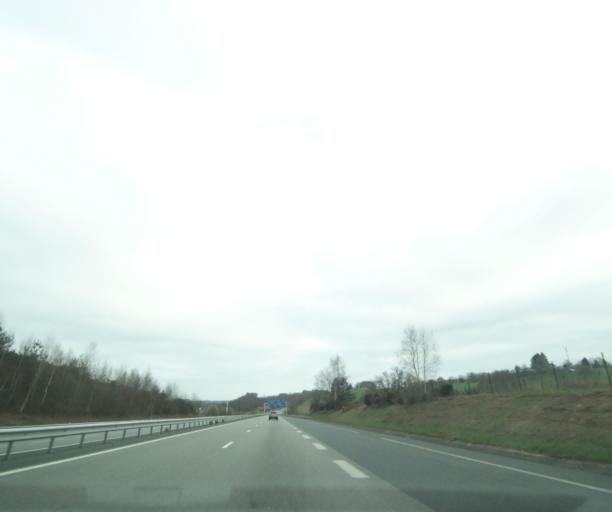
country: FR
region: Limousin
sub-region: Departement de la Correze
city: Saint-Mexant
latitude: 45.3168
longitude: 1.5742
